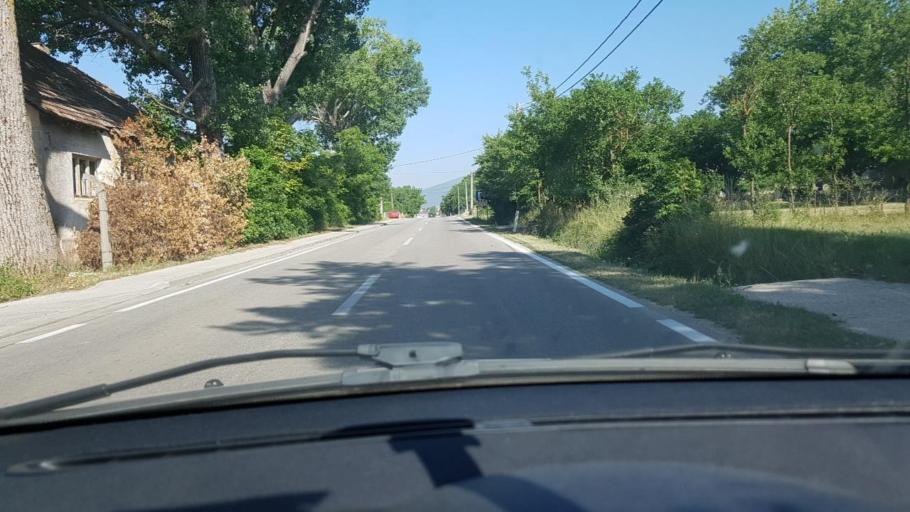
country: BA
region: Federation of Bosnia and Herzegovina
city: Livno
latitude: 43.8378
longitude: 16.9782
